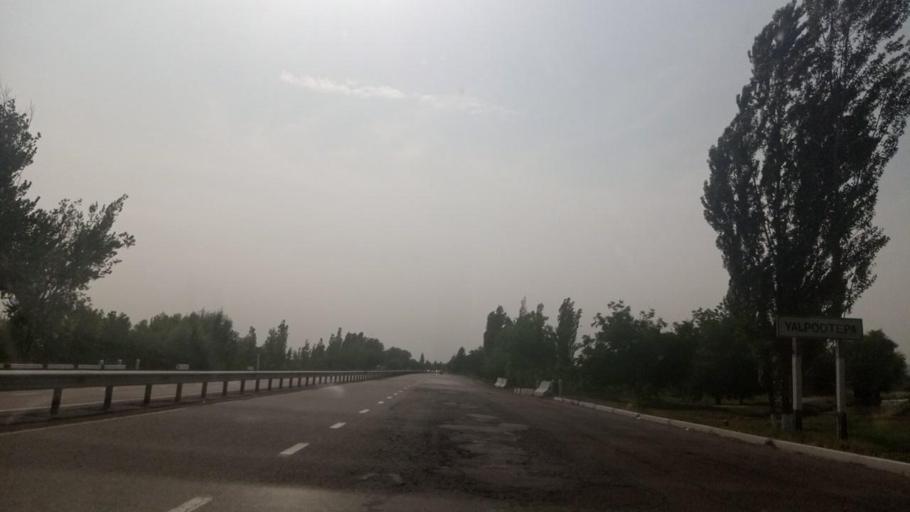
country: UZ
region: Toshkent
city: Ohangaron
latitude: 40.9087
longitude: 69.7795
